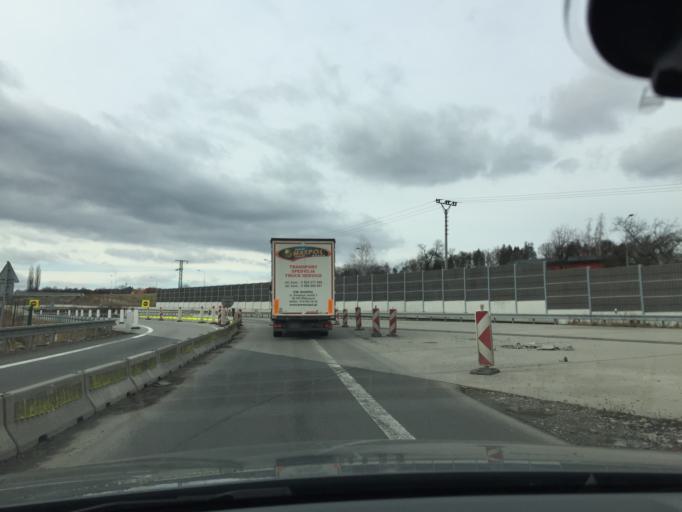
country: CZ
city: Sviadnov
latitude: 49.6681
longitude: 18.3099
